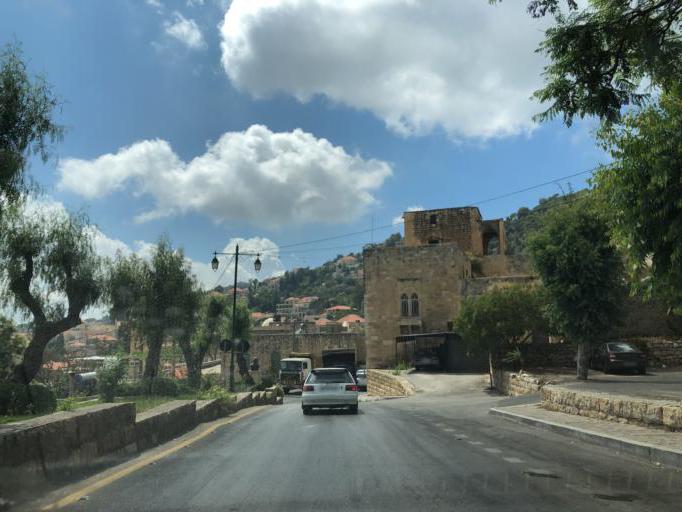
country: LB
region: Mont-Liban
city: Beit ed Dine
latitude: 33.6972
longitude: 35.5665
